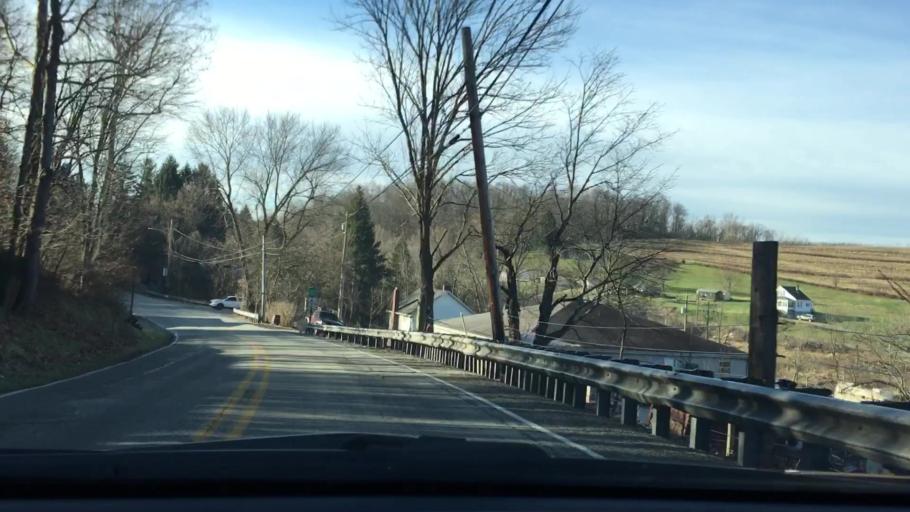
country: US
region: Pennsylvania
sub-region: Westmoreland County
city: Irwin
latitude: 40.2740
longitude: -79.6995
